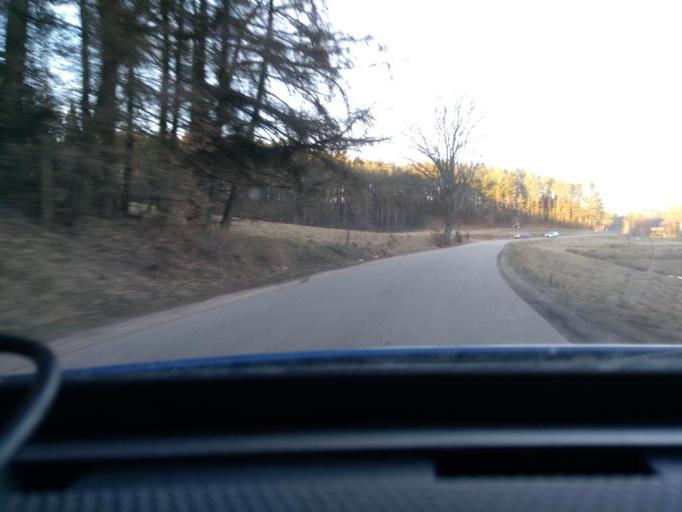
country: PL
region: Pomeranian Voivodeship
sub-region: Powiat kartuski
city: Przodkowo
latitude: 54.3809
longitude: 18.2659
